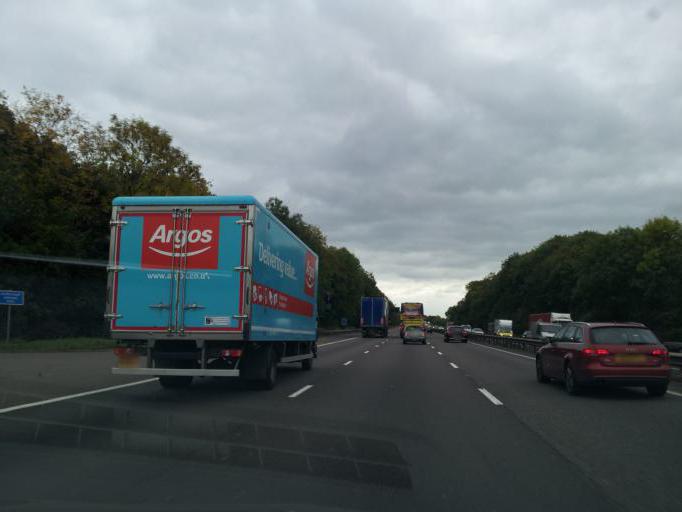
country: GB
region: England
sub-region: Northamptonshire
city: Hartwell
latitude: 52.1456
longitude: -0.8391
